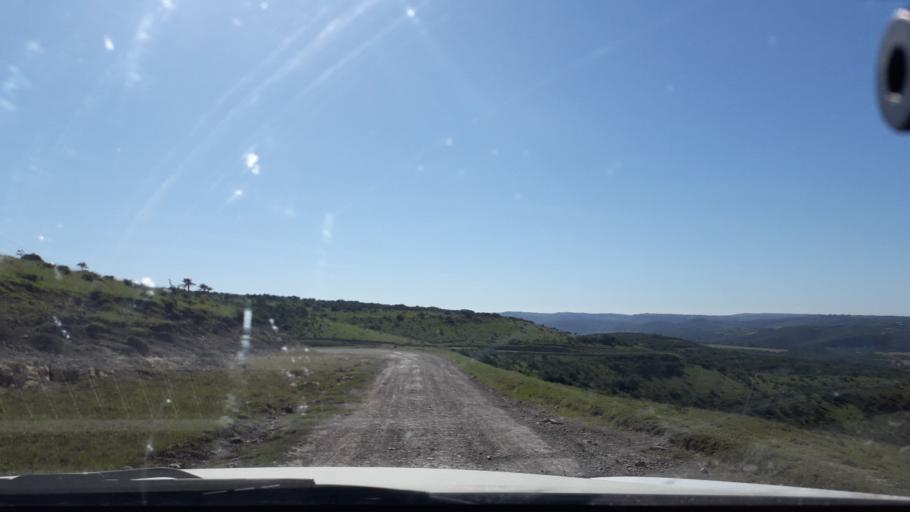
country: ZA
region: Eastern Cape
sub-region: Amathole District Municipality
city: Komga
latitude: -32.7902
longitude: 27.9527
